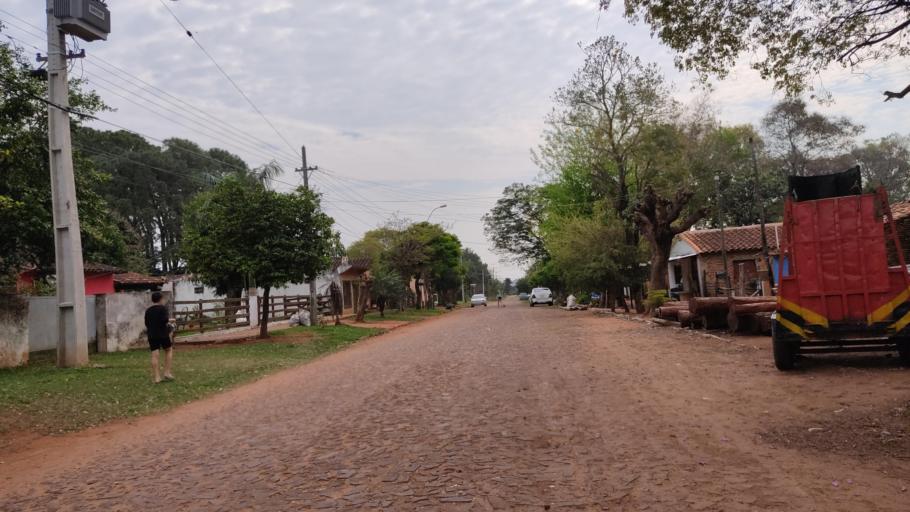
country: PY
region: Misiones
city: San Juan Bautista
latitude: -26.6670
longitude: -57.1531
